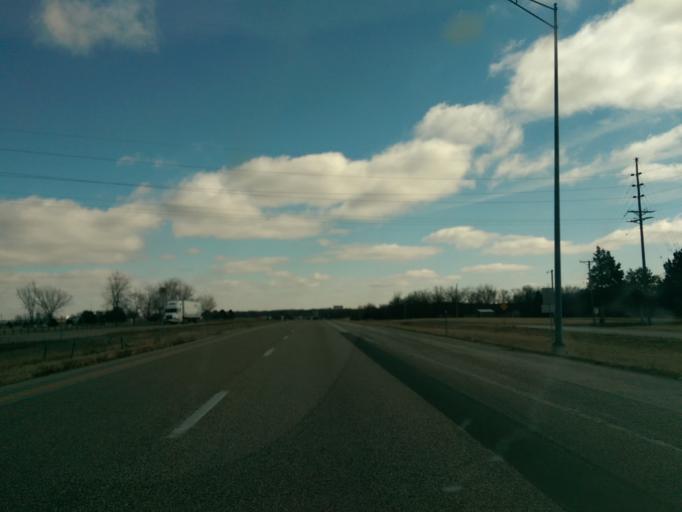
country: US
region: Missouri
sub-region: Montgomery County
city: Montgomery City
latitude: 38.8719
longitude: -91.3687
